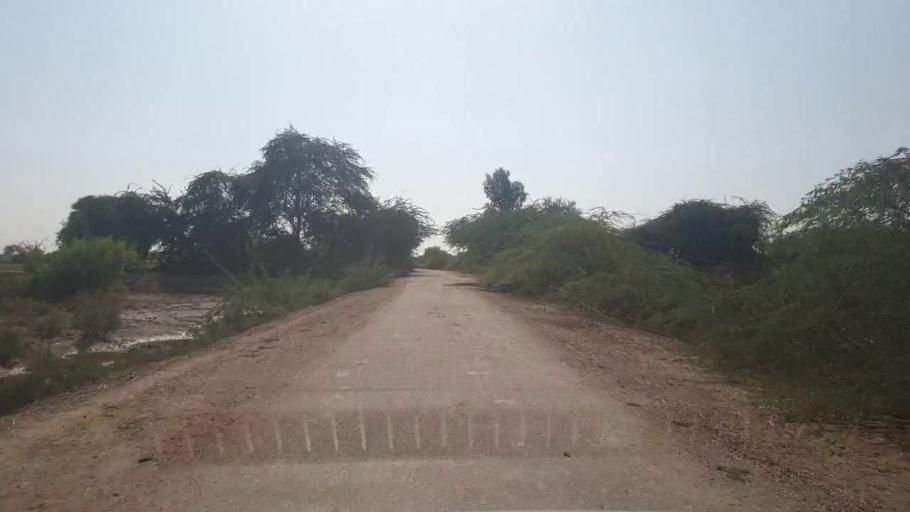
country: PK
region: Sindh
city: Badin
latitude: 24.5506
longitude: 68.8127
